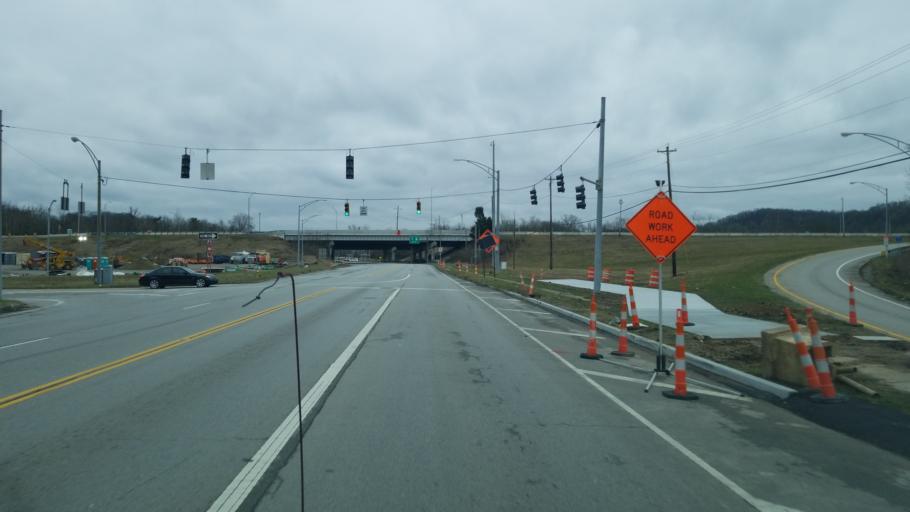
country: US
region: Kentucky
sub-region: Campbell County
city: Fort Thomas
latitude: 39.0627
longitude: -84.4226
